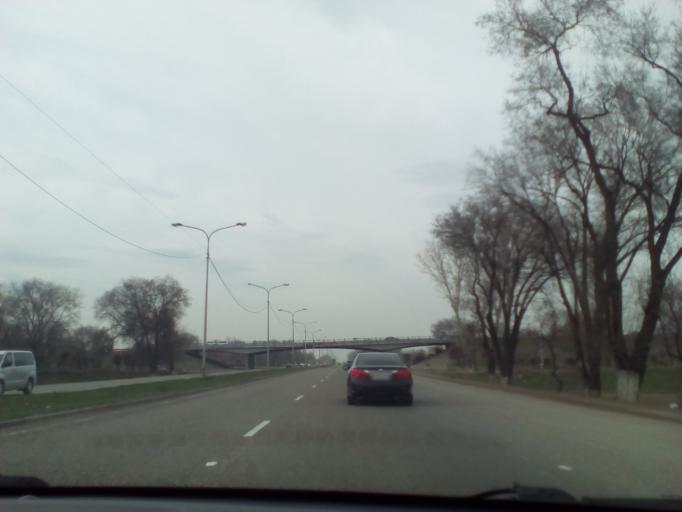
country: KZ
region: Almaty Oblysy
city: Burunday
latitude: 43.2179
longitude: 76.6512
